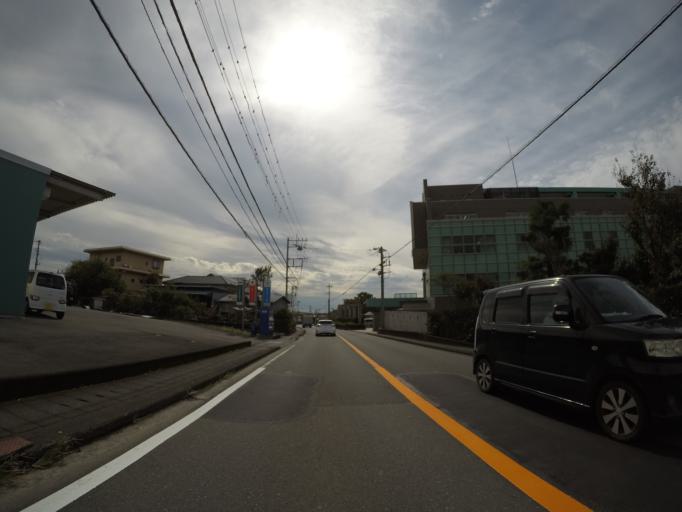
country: JP
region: Shizuoka
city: Fuji
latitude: 35.2055
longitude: 138.6844
